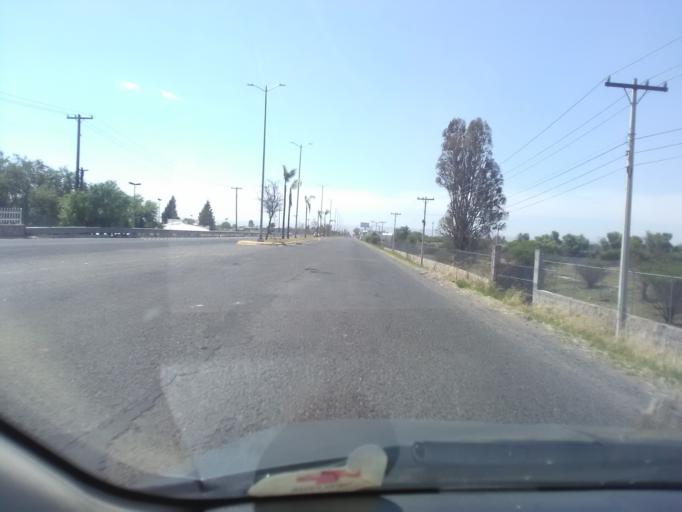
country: MX
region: Durango
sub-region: Durango
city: Jose Refugio Salcido
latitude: 24.0258
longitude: -104.5688
